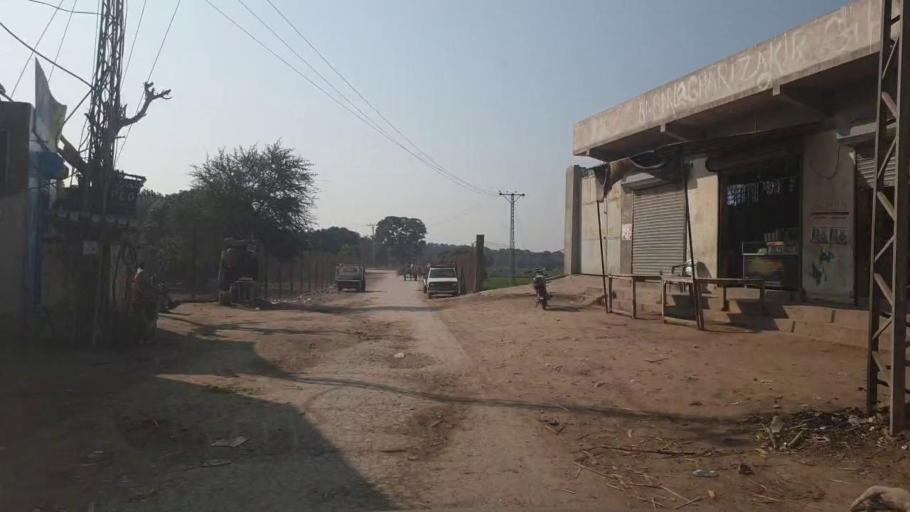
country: PK
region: Sindh
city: Tando Allahyar
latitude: 25.4780
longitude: 68.7727
